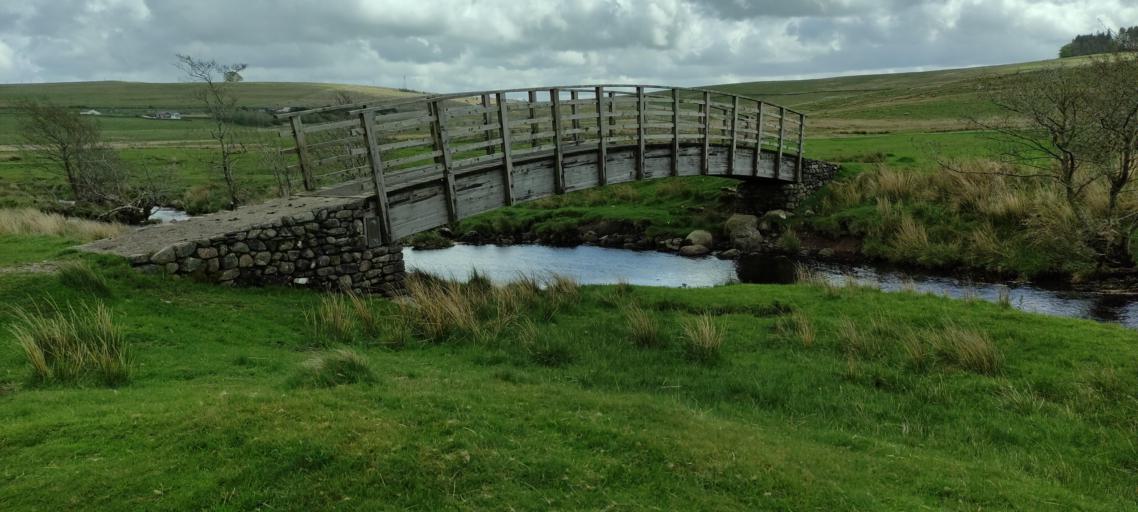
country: GB
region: England
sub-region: Cumbria
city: Penrith
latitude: 54.5034
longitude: -2.6842
